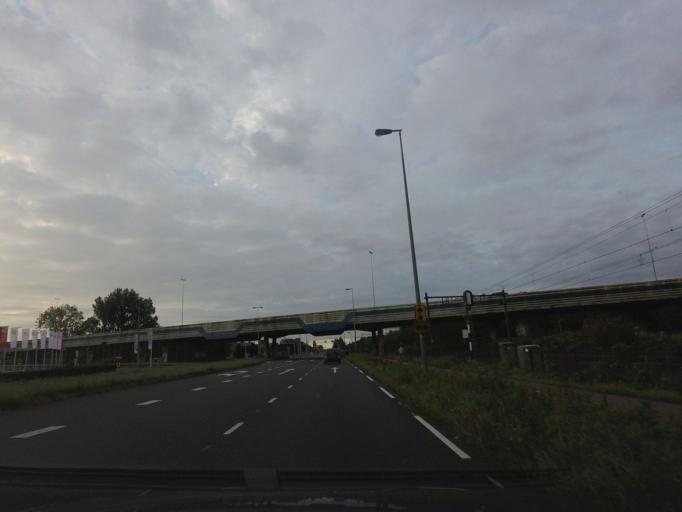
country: NL
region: North Holland
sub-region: Gemeente Zaanstad
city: Zaanstad
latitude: 52.4653
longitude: 4.8056
